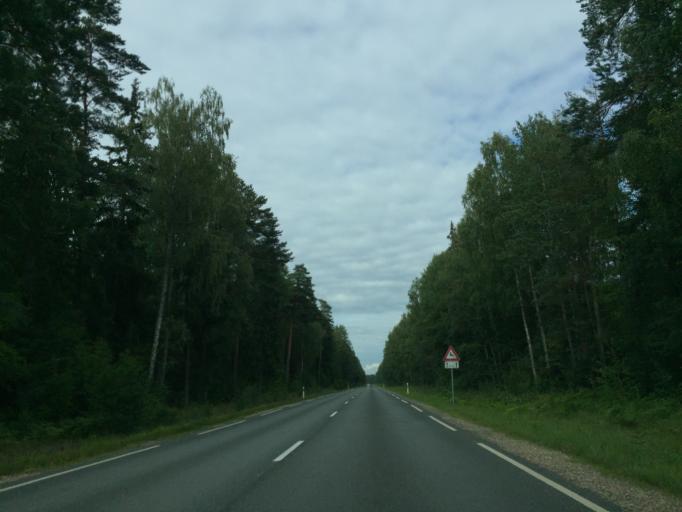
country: LV
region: Carnikava
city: Carnikava
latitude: 57.1050
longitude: 24.2140
